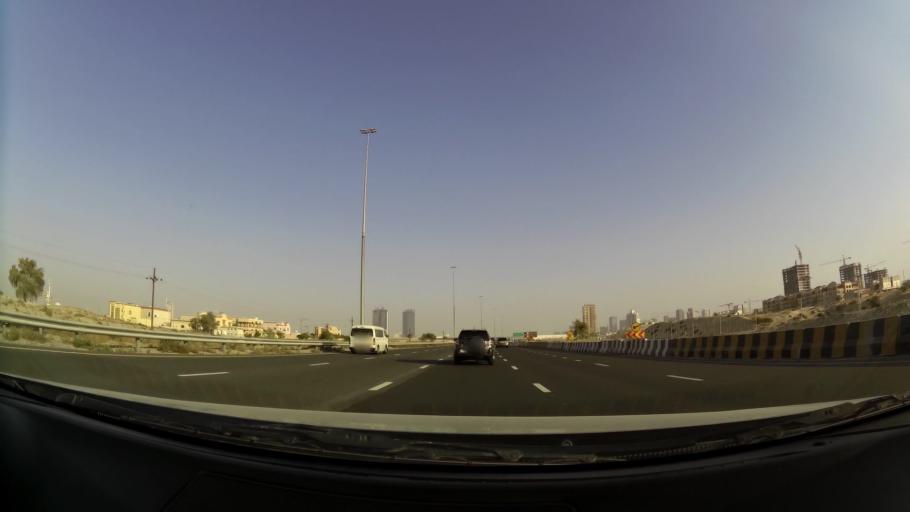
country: AE
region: Dubai
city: Dubai
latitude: 25.0657
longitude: 55.2199
